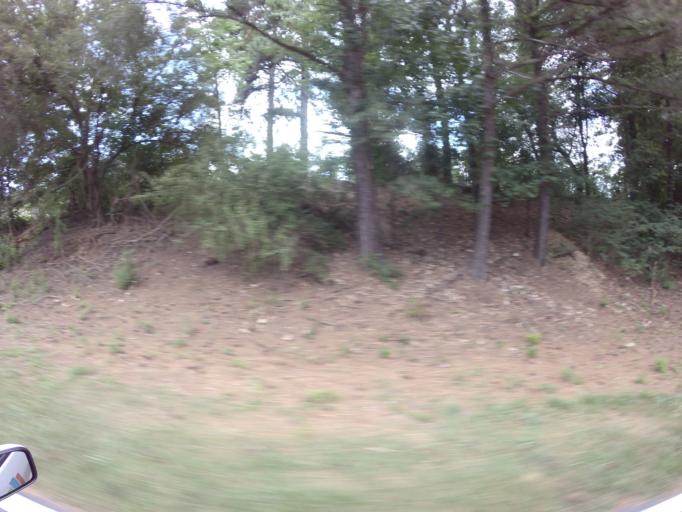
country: US
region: Georgia
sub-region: Fulton County
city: Johns Creek
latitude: 34.0010
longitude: -84.2568
